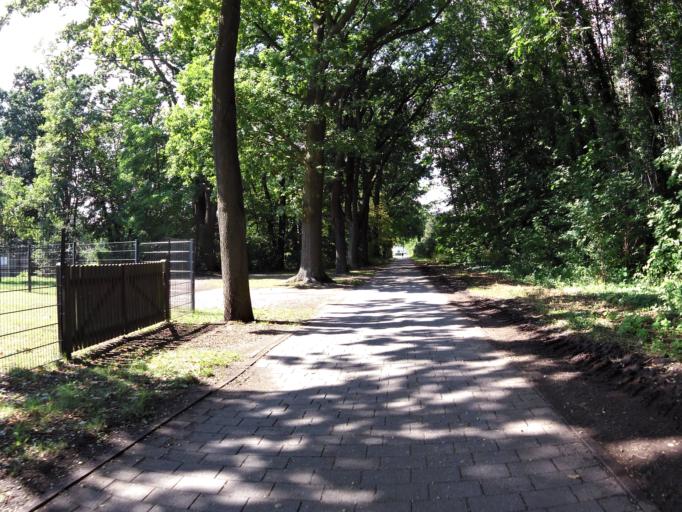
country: DE
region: Brandenburg
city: Storkow
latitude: 52.2405
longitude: 13.9088
